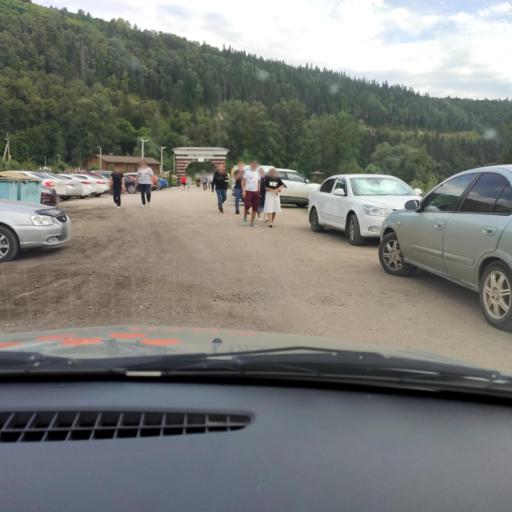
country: RU
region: Bashkortostan
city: Krasnyy Klyuch
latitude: 55.3778
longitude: 56.6767
